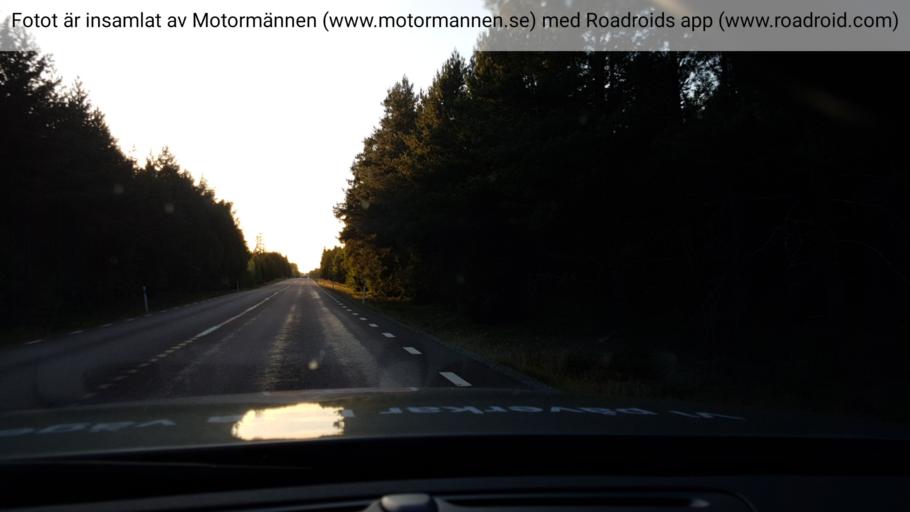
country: SE
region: Vaermland
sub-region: Storfors Kommun
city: Storfors
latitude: 59.4583
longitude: 14.3618
